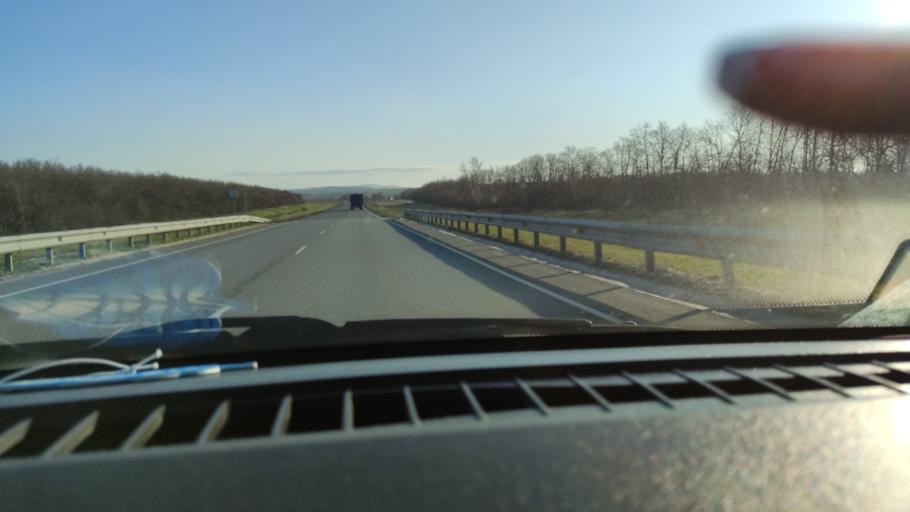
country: RU
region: Saratov
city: Balakovo
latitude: 52.1046
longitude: 47.7411
